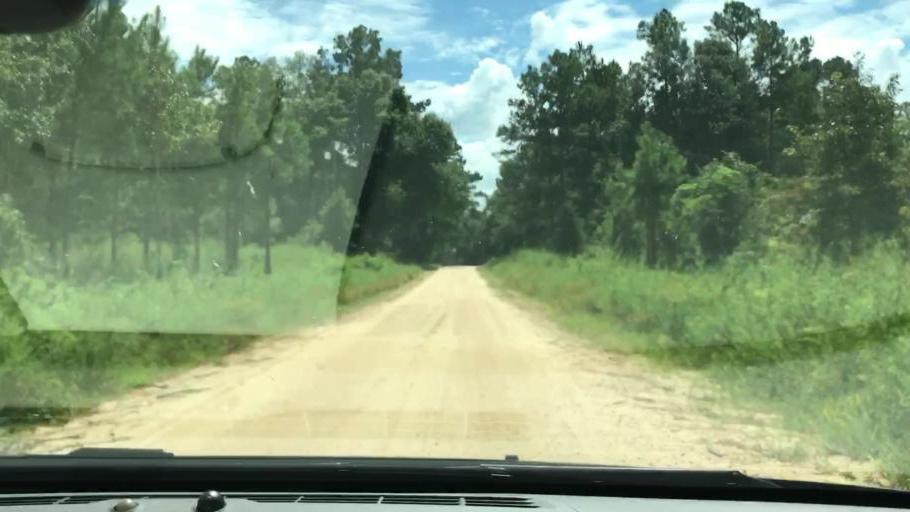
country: US
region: Georgia
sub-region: Quitman County
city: Georgetown
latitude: 32.0274
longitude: -85.0368
